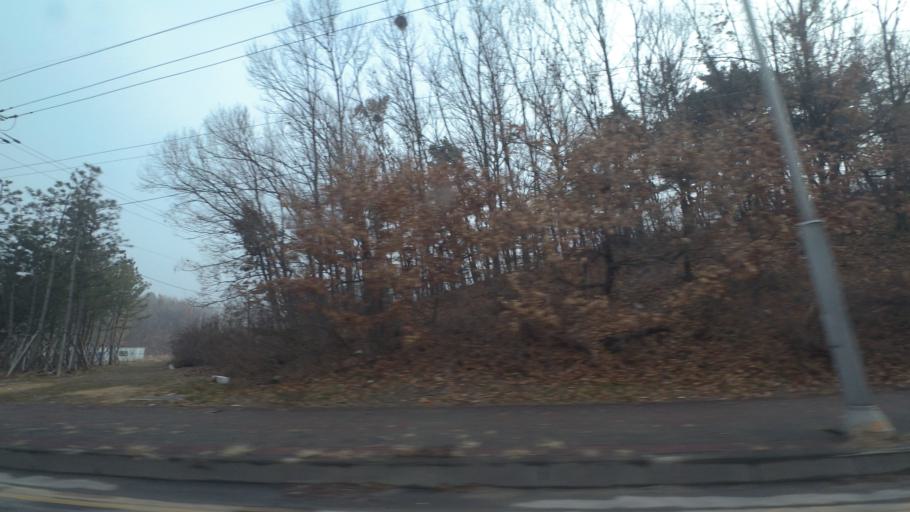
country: KR
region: Gyeonggi-do
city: Hwaseong-si
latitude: 36.9902
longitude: 126.8521
